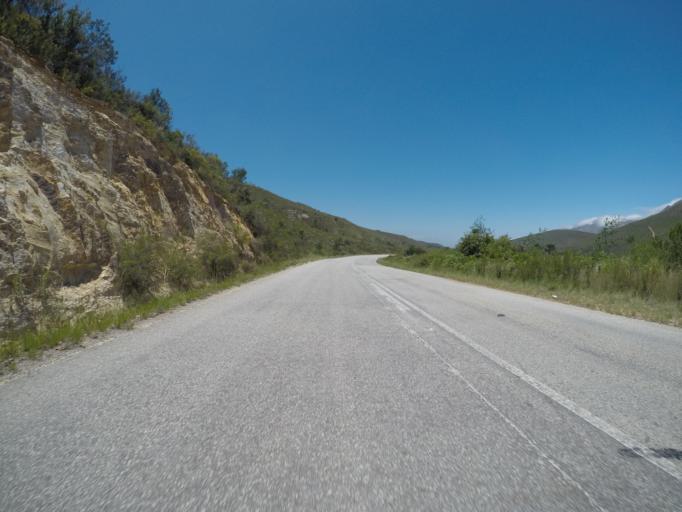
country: ZA
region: Eastern Cape
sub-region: Cacadu District Municipality
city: Kareedouw
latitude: -33.8667
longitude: 24.0192
